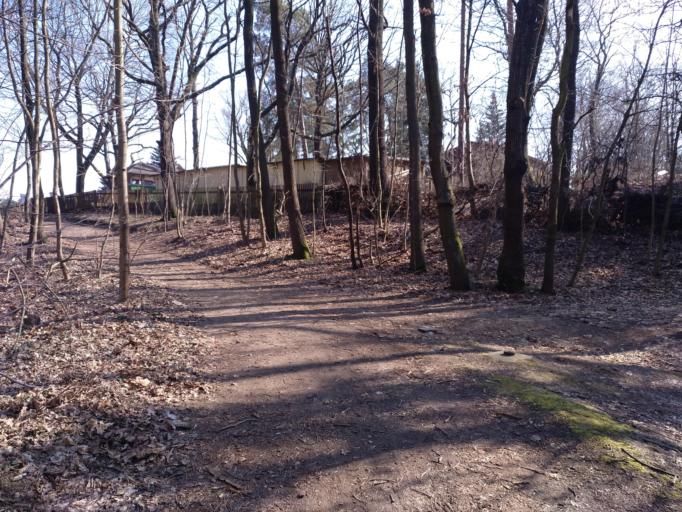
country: DE
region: Saxony
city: Albertstadt
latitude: 51.1123
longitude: 13.7182
